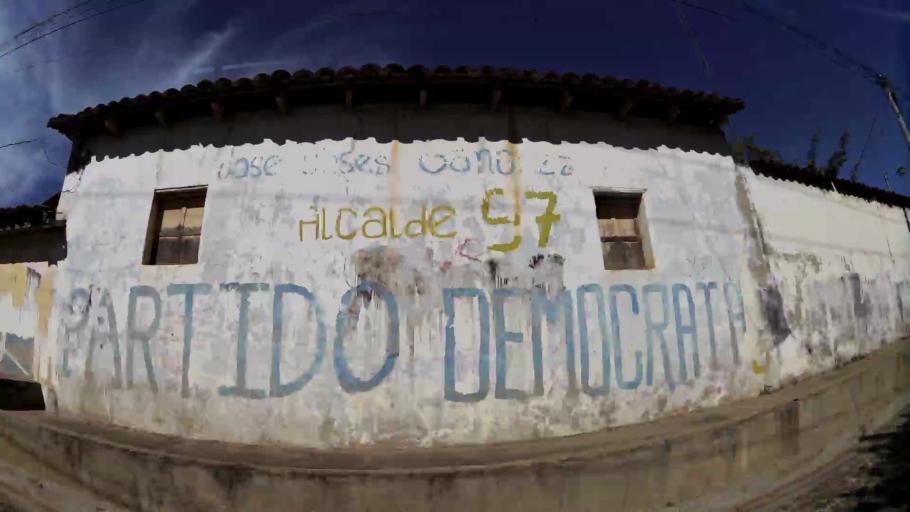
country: SV
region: Cuscatlan
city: Suchitoto
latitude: 13.9313
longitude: -89.0309
